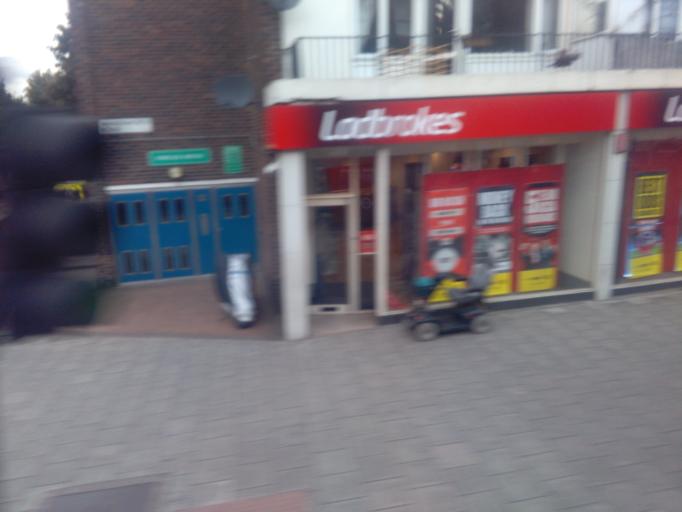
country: GB
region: England
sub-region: Greater London
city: Battersea
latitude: 51.4737
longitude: -0.1334
